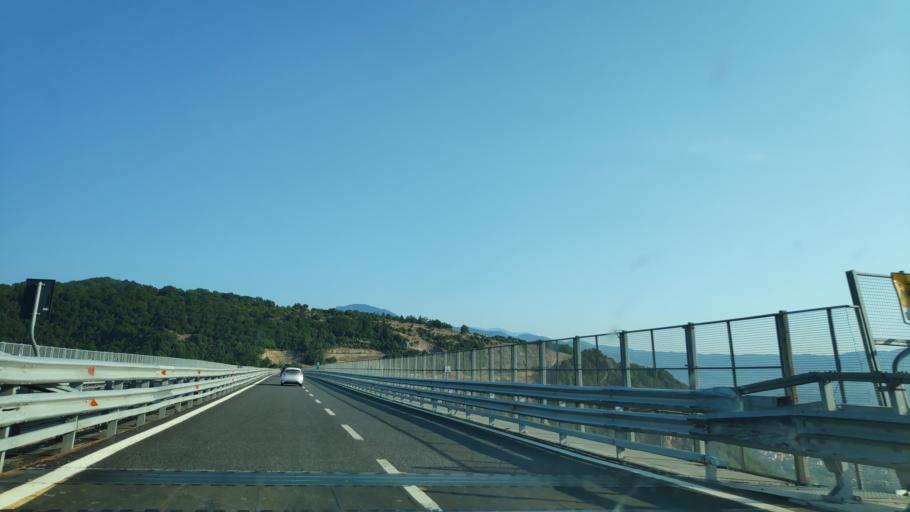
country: IT
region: Calabria
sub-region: Provincia di Cosenza
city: Laino Castello-Nuovo Centro
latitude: 39.9370
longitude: 15.9601
